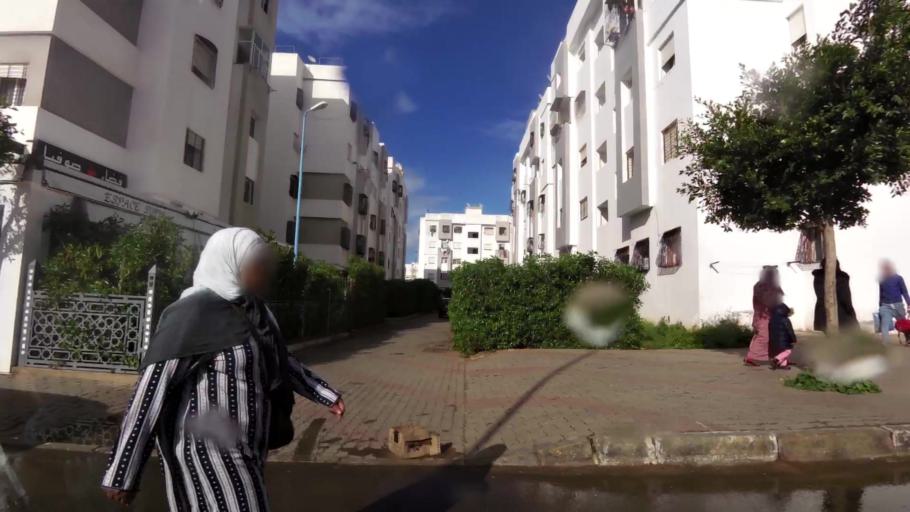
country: MA
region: Grand Casablanca
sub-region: Casablanca
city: Casablanca
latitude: 33.5552
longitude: -7.7016
